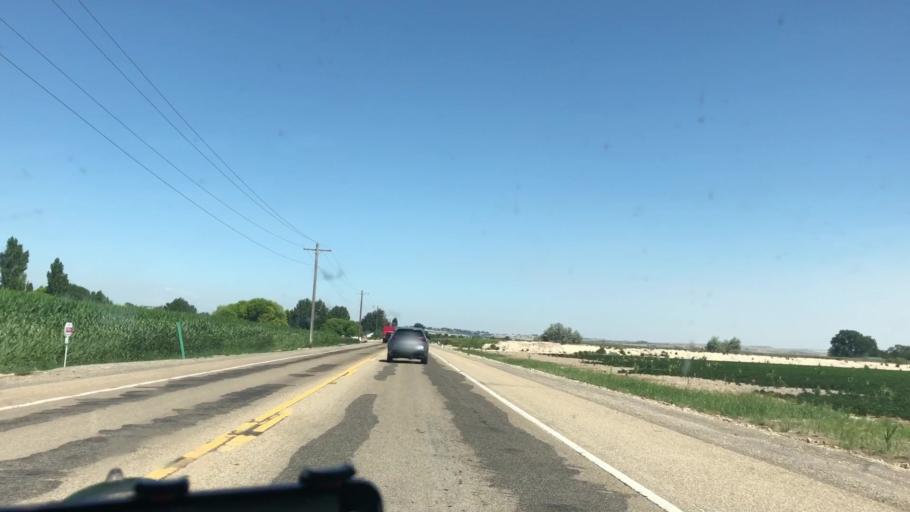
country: US
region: Idaho
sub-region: Owyhee County
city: Marsing
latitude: 43.5453
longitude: -116.8445
